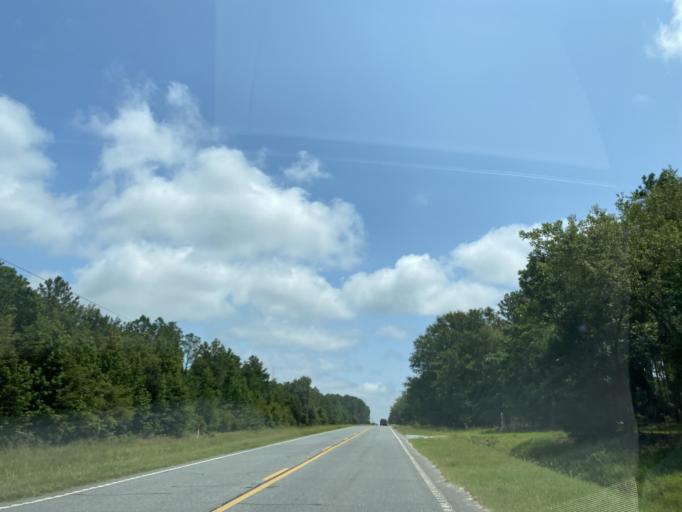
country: US
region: Georgia
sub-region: Telfair County
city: McRae
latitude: 32.1025
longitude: -82.8376
